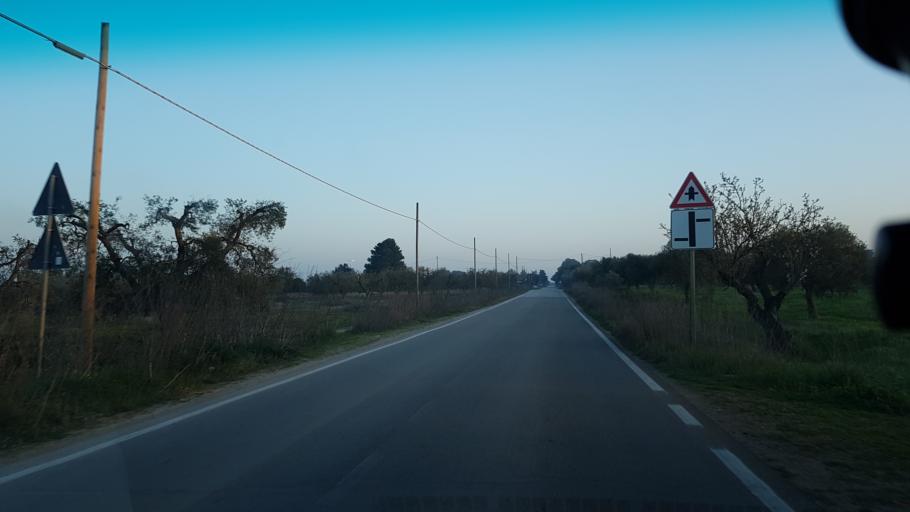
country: IT
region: Apulia
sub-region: Provincia di Brindisi
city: San Vito dei Normanni
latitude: 40.6469
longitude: 17.7761
